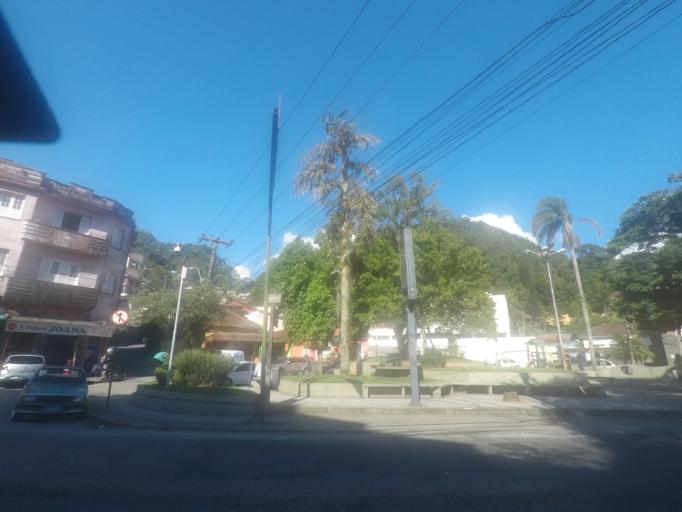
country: BR
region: Rio de Janeiro
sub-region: Petropolis
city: Petropolis
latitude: -22.5227
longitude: -43.1834
